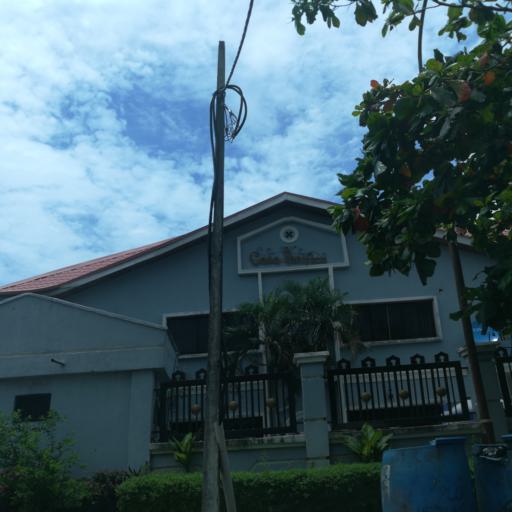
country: NG
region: Lagos
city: Ikoyi
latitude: 6.4385
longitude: 3.4677
